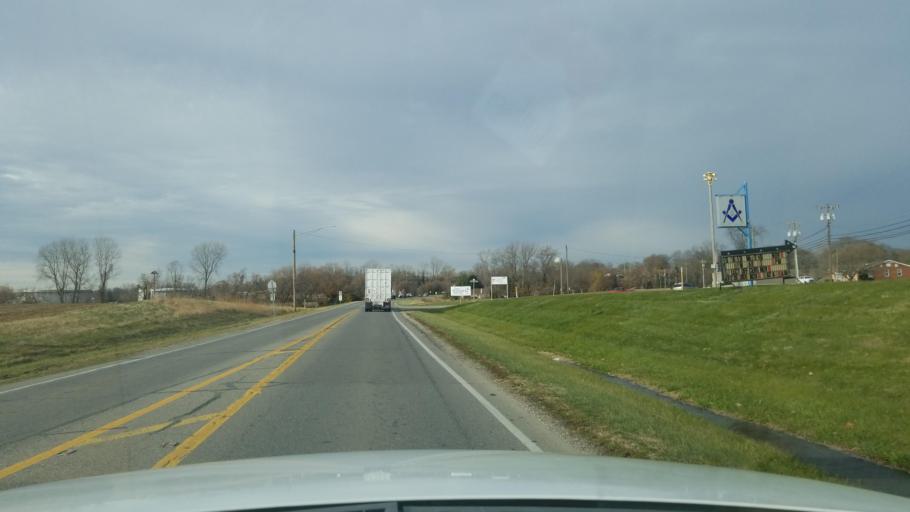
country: US
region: Indiana
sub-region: Posey County
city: Mount Vernon
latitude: 37.9287
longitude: -87.9094
